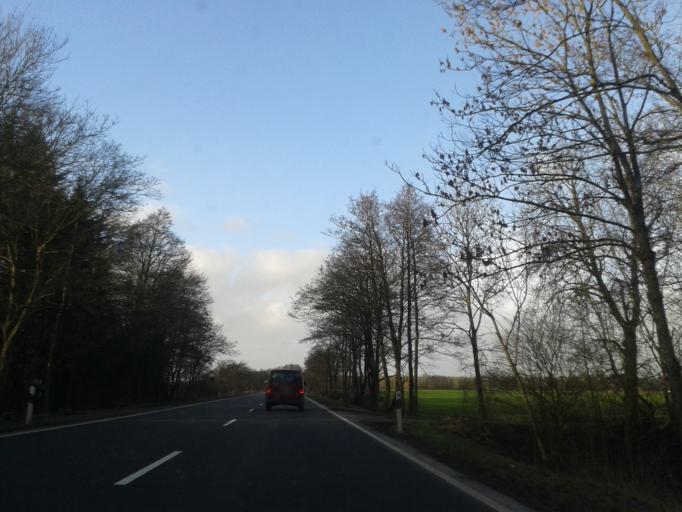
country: DE
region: Lower Saxony
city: Osteel
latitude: 53.5590
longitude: 7.2512
